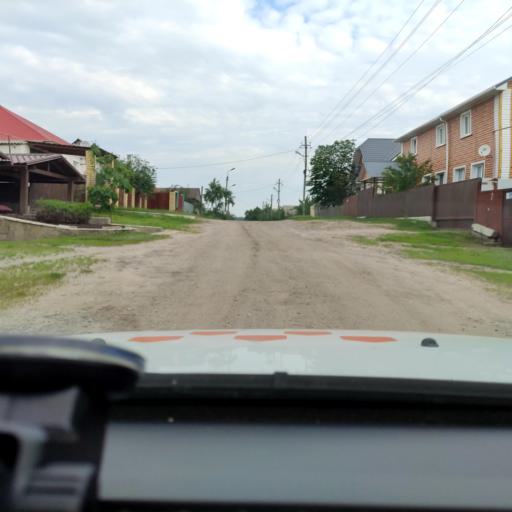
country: RU
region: Voronezj
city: Maslovka
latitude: 51.5794
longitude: 39.3090
